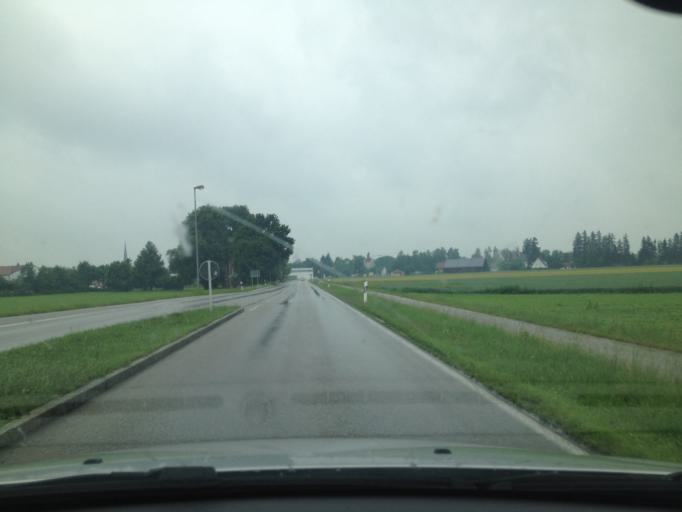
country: DE
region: Bavaria
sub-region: Swabia
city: Schwabmunchen
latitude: 48.1729
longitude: 10.7706
